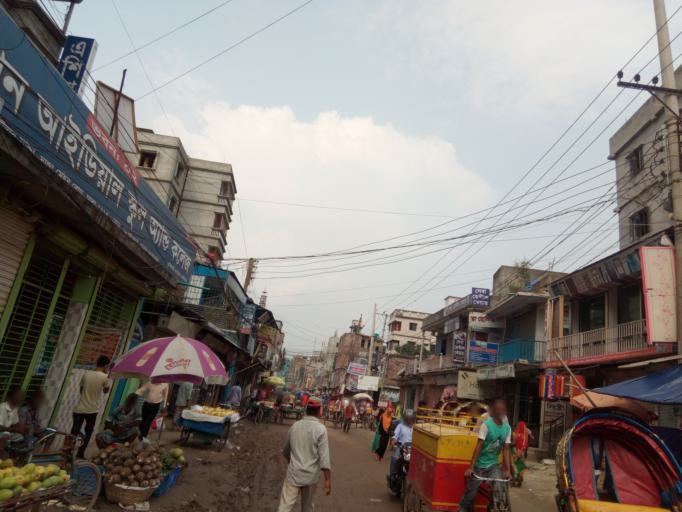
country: BD
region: Dhaka
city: Paltan
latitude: 23.7294
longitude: 90.4373
